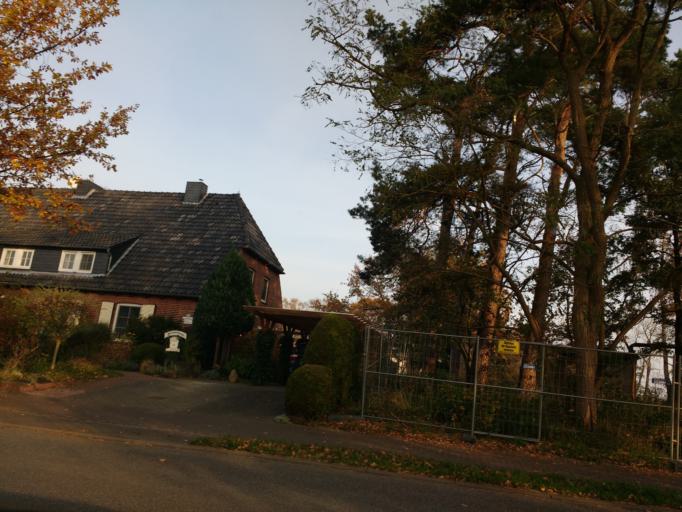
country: DE
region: Mecklenburg-Vorpommern
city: Ostseebad Boltenhagen
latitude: 53.9797
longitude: 11.2347
